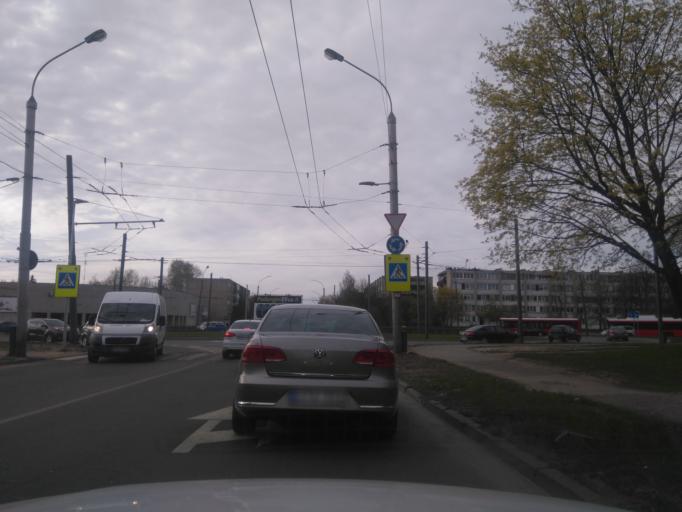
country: LT
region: Kauno apskritis
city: Dainava (Kaunas)
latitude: 54.9184
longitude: 23.9714
